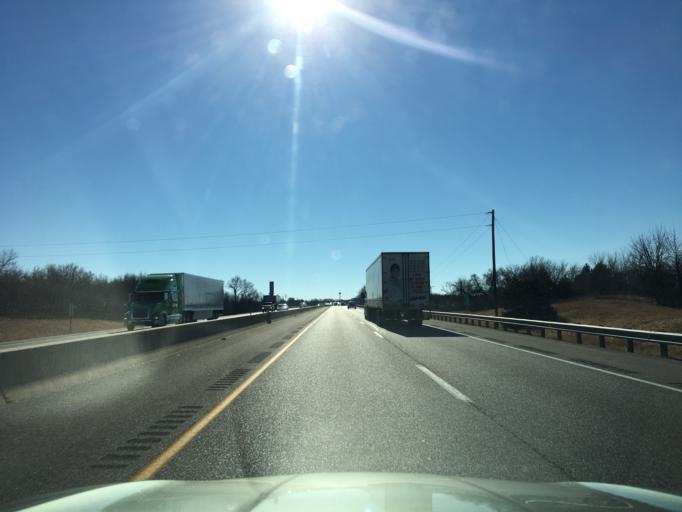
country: US
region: Kansas
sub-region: Sumner County
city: Belle Plaine
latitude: 37.3856
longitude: -97.3247
